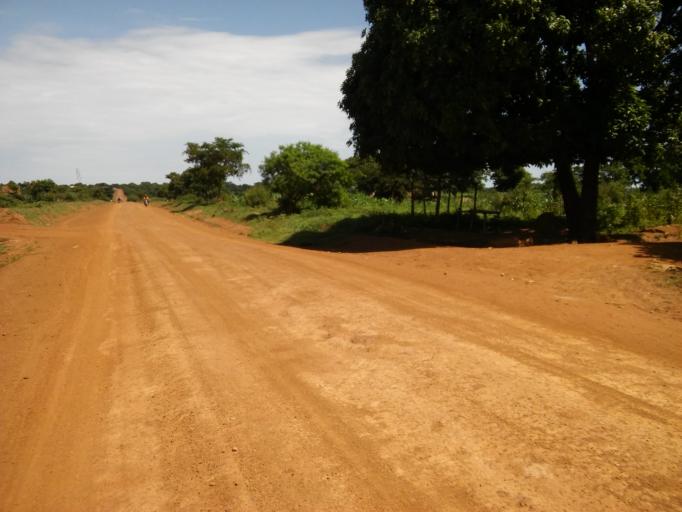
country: UG
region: Eastern Region
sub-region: Kumi District
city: Kumi
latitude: 1.4819
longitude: 33.9023
